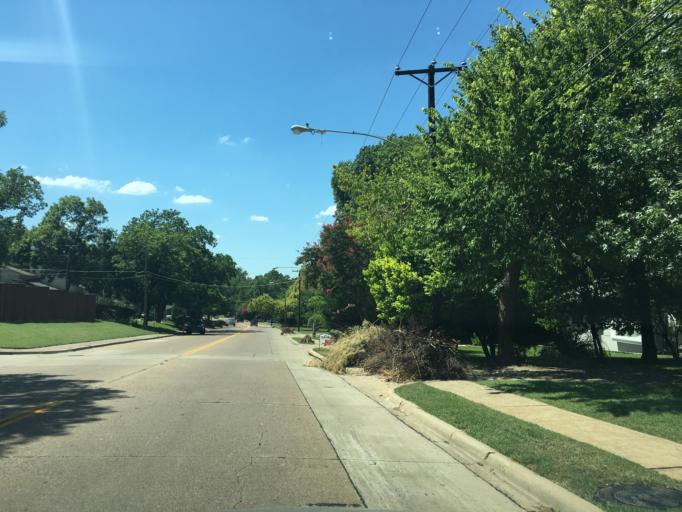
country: US
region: Texas
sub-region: Dallas County
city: Highland Park
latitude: 32.8421
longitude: -96.7003
